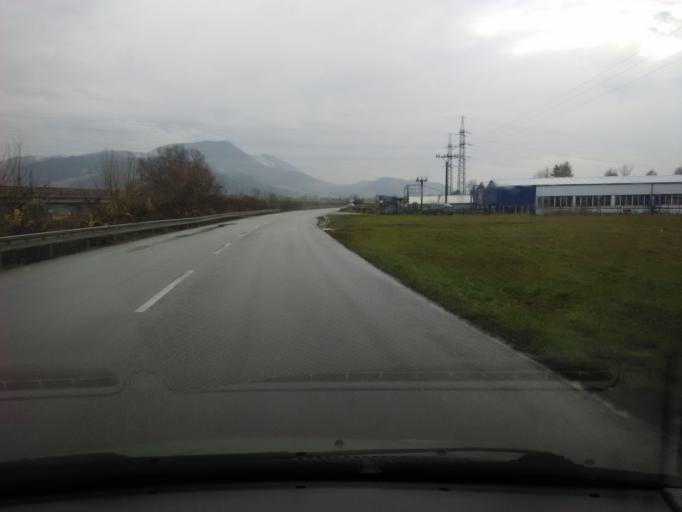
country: SK
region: Zilinsky
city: Bytca
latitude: 49.1926
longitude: 18.5121
